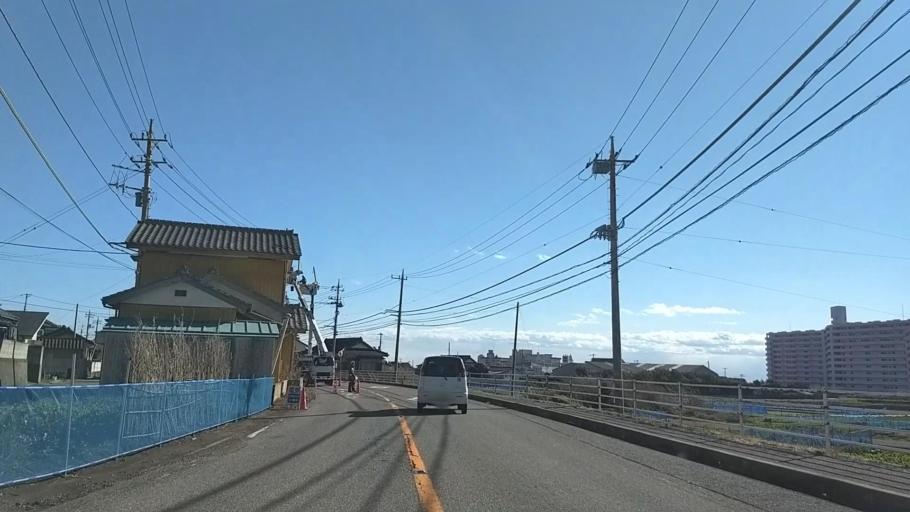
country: JP
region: Chiba
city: Tateyama
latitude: 34.9073
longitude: 139.8804
